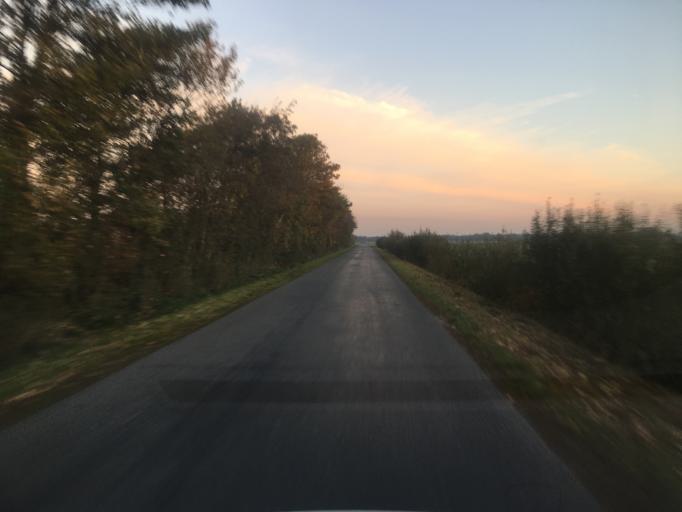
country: DE
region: Schleswig-Holstein
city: Bramstedtlund
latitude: 54.9760
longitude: 9.0681
